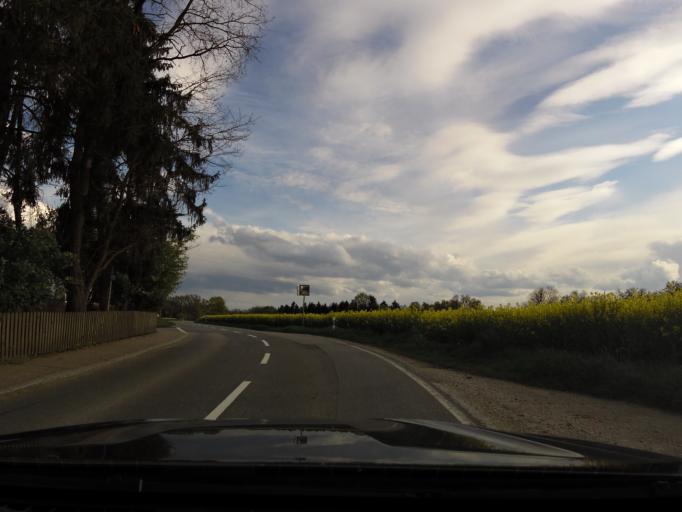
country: DE
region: Bavaria
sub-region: Upper Bavaria
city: Wang
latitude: 48.4945
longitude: 11.9233
